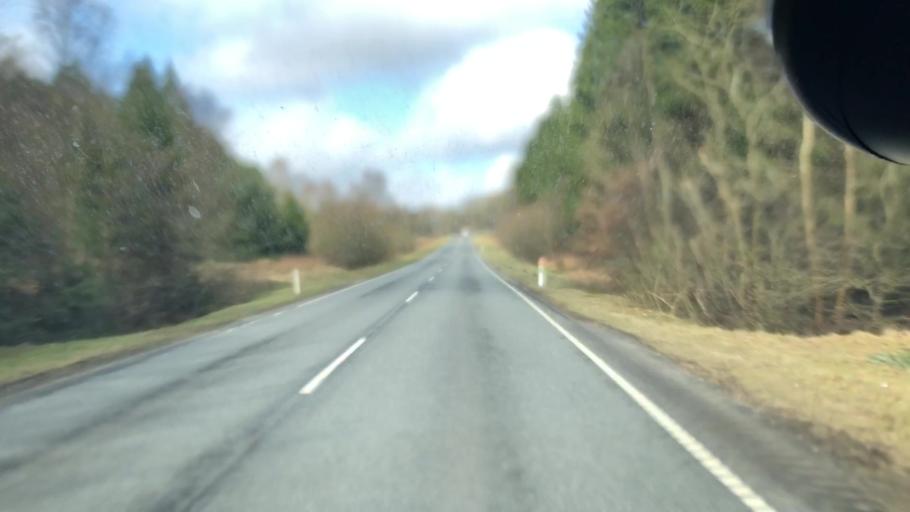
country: DK
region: Central Jutland
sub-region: Silkeborg Kommune
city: Virklund
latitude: 56.0745
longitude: 9.5721
